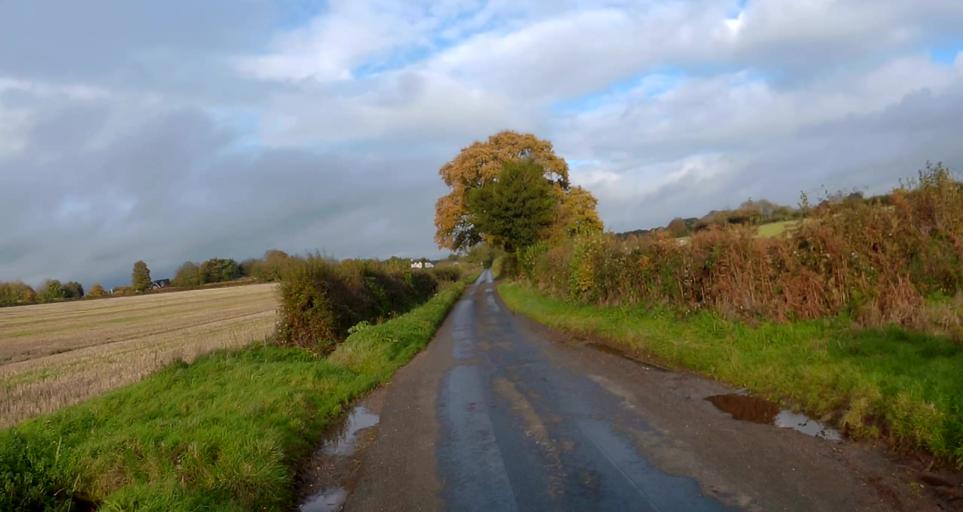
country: GB
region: England
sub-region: Hampshire
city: Four Marks
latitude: 51.1417
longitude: -1.0986
